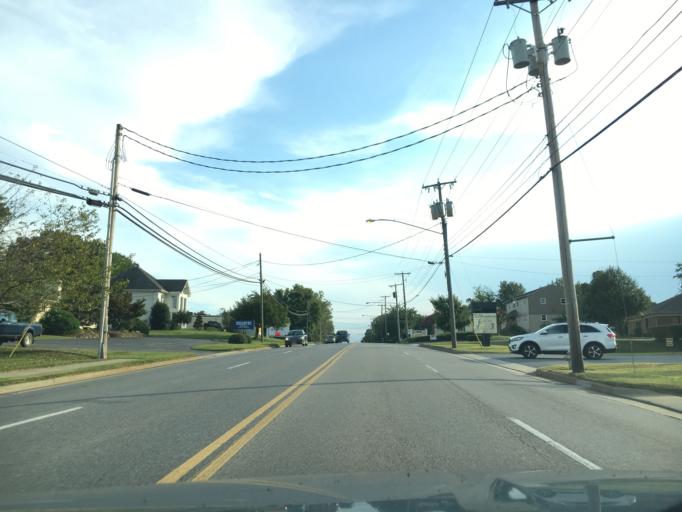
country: US
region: Virginia
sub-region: City of Lynchburg
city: West Lynchburg
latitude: 37.4055
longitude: -79.2203
